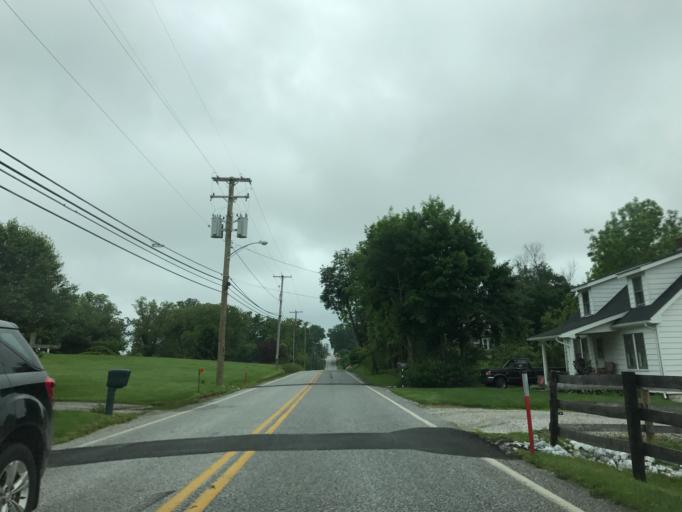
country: US
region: Pennsylvania
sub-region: York County
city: Susquehanna Trails
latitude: 39.7347
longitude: -76.4516
